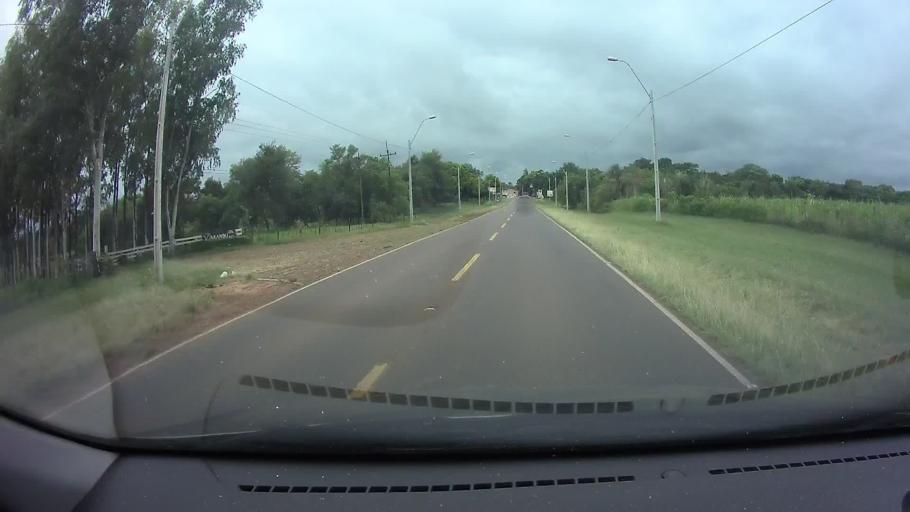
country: PY
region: Central
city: Nueva Italia
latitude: -25.6043
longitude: -57.4873
